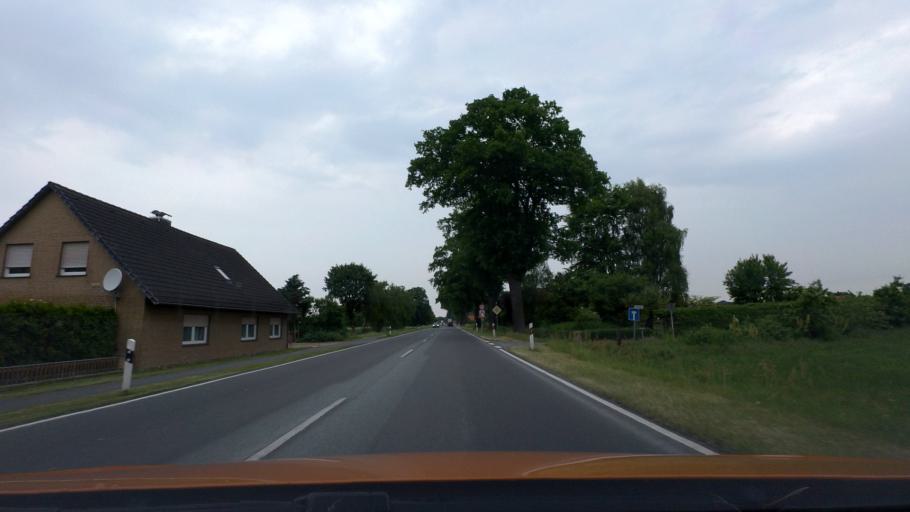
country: DE
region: Lower Saxony
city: Asendorf
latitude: 52.7490
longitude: 9.0205
